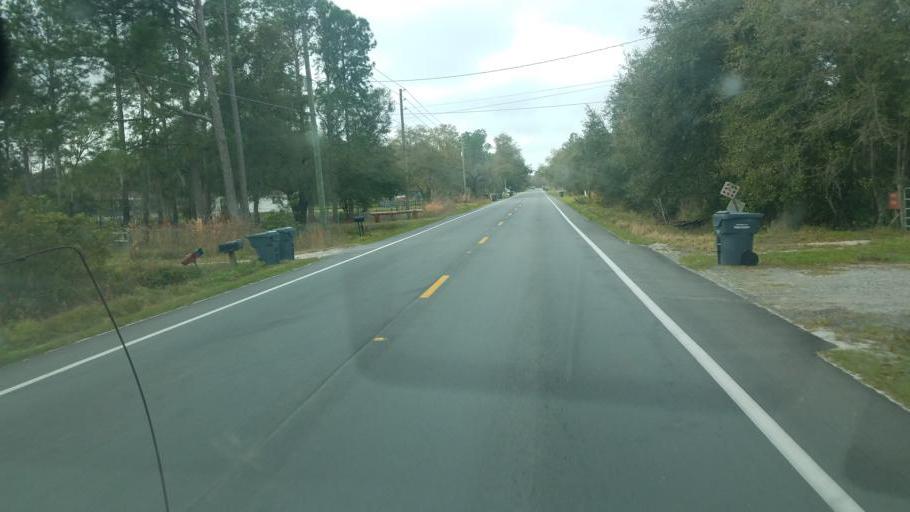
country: US
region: Florida
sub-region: Polk County
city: Kathleen
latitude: 28.2055
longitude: -81.9886
